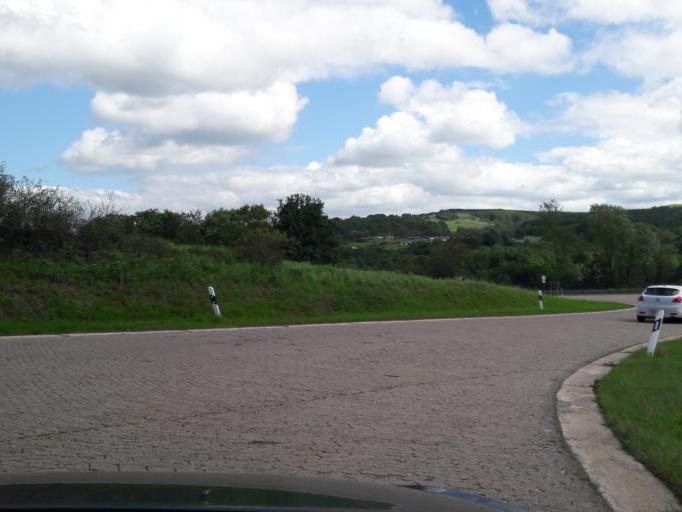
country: DE
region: Rheinland-Pfalz
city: Reichenbach
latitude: 49.6450
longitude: 7.2947
